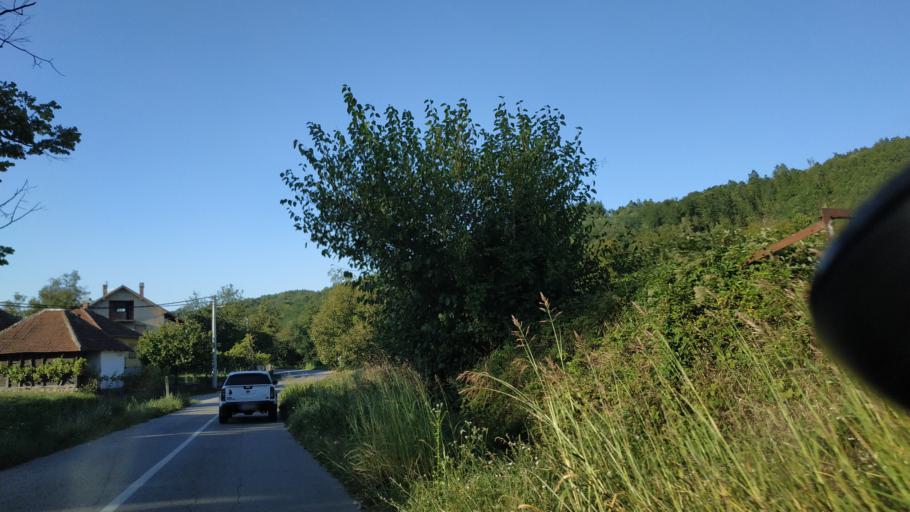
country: RS
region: Central Serbia
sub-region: Rasinski Okrug
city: Krusevac
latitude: 43.4798
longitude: 21.3533
